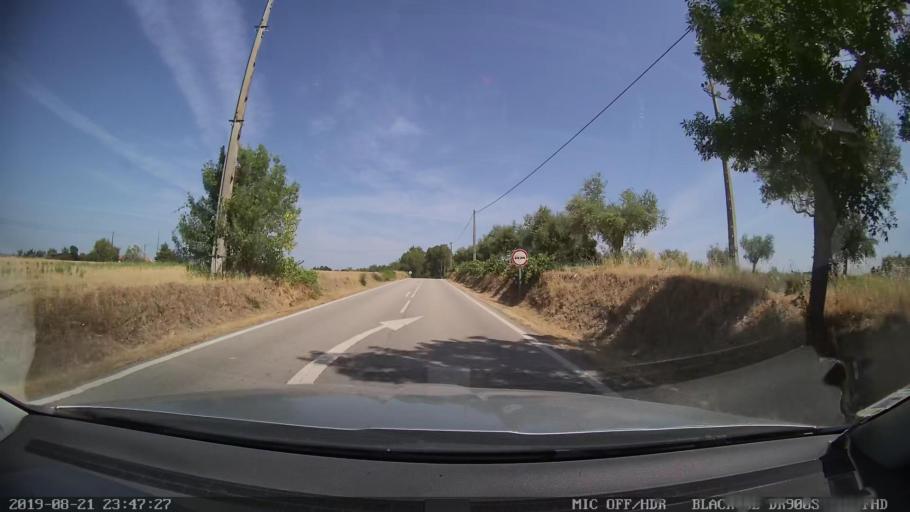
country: PT
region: Castelo Branco
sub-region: Idanha-A-Nova
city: Idanha-a-Nova
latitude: 39.8522
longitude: -7.2574
